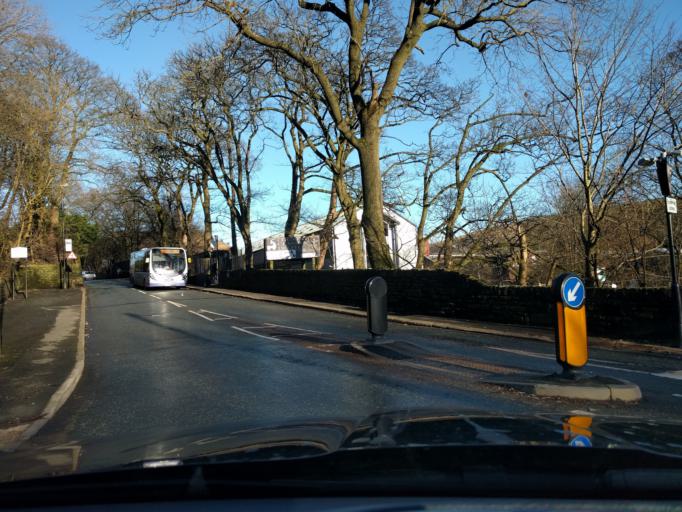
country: GB
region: England
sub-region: Borough of Oldham
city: Delph
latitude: 53.5640
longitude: -2.0209
